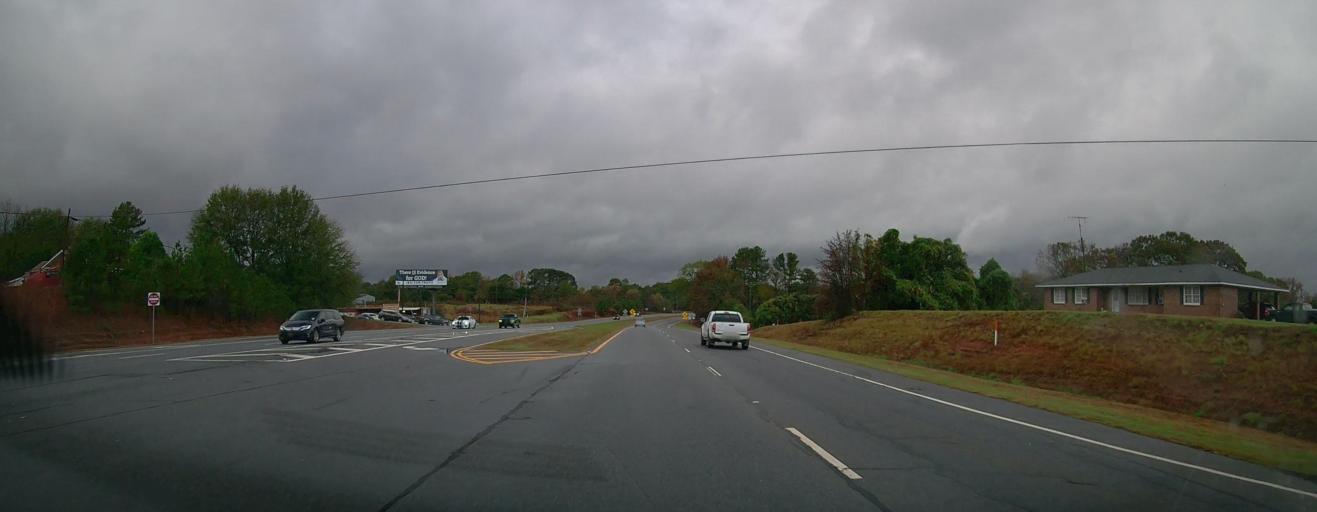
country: US
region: Georgia
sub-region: Jackson County
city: Nicholson
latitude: 34.0973
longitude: -83.4311
